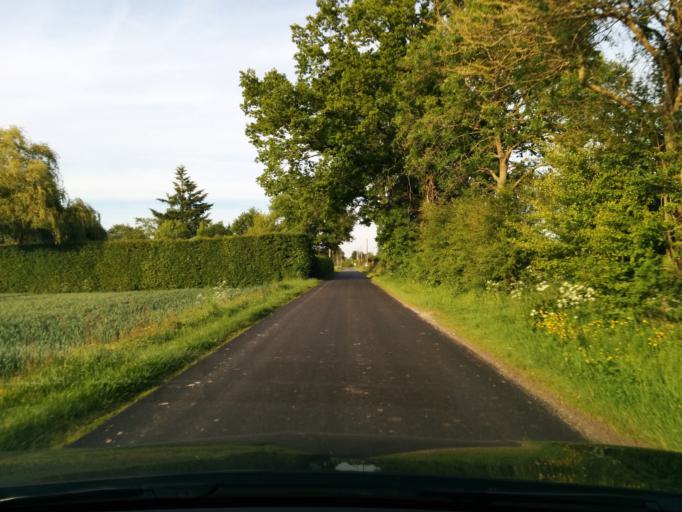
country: FR
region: Haute-Normandie
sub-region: Departement de la Seine-Maritime
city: Neufchatel-en-Bray
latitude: 49.6676
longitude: 1.4707
